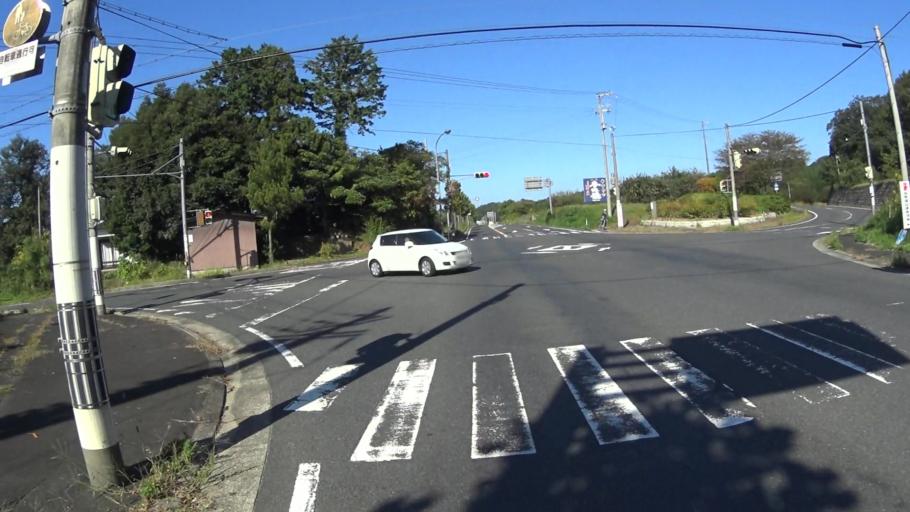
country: JP
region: Hyogo
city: Toyooka
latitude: 35.6269
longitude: 134.9291
